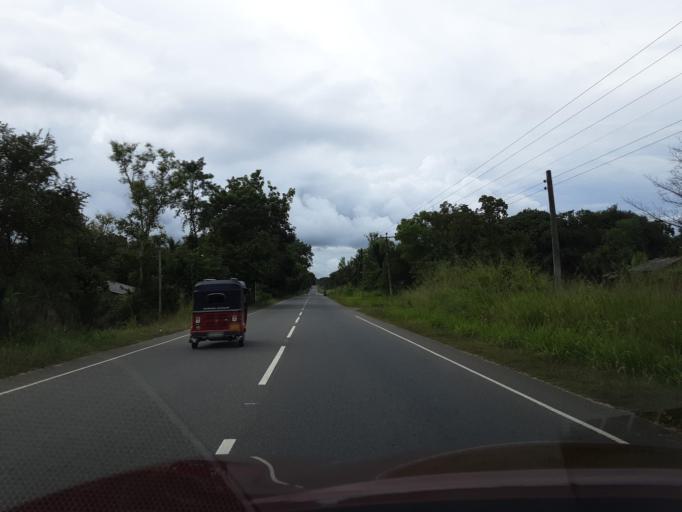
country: LK
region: Uva
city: Badulla
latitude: 7.3905
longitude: 81.1369
